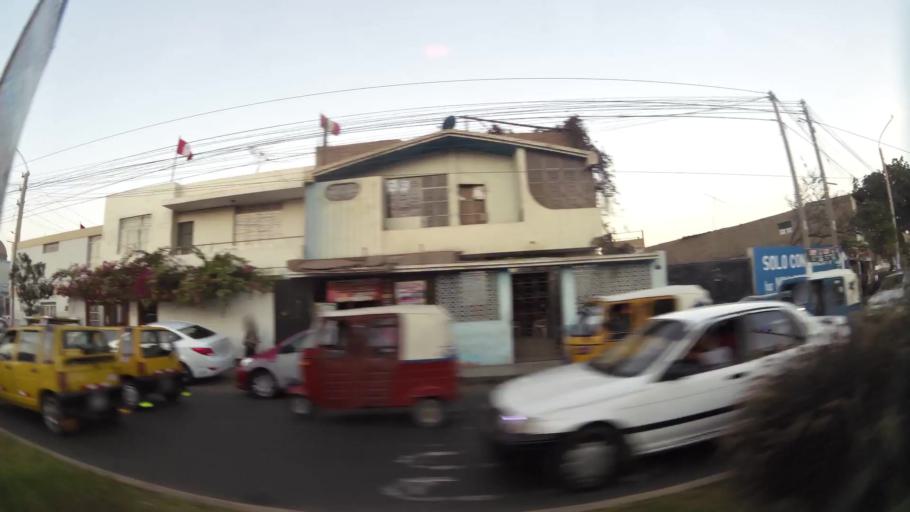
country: PE
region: Ica
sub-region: Provincia de Ica
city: Ica
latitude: -14.0655
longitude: -75.7324
